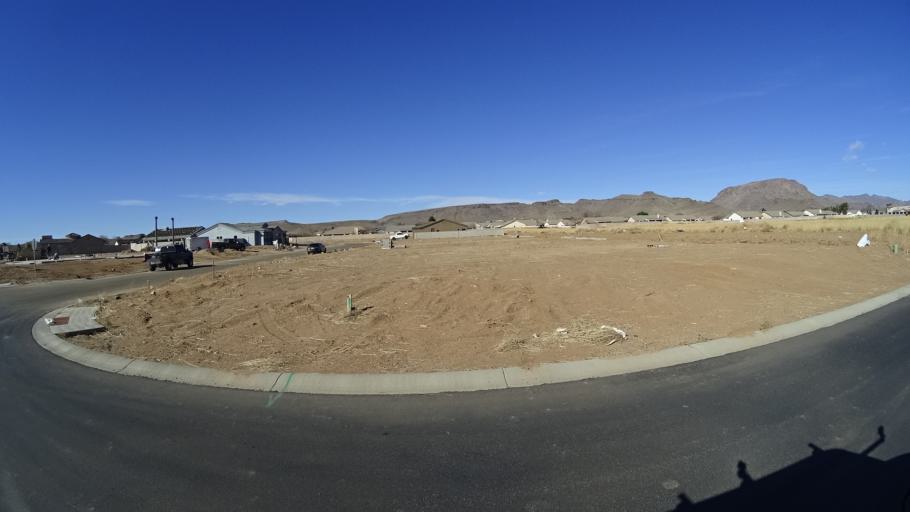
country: US
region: Arizona
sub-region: Mohave County
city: New Kingman-Butler
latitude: 35.2364
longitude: -114.0259
